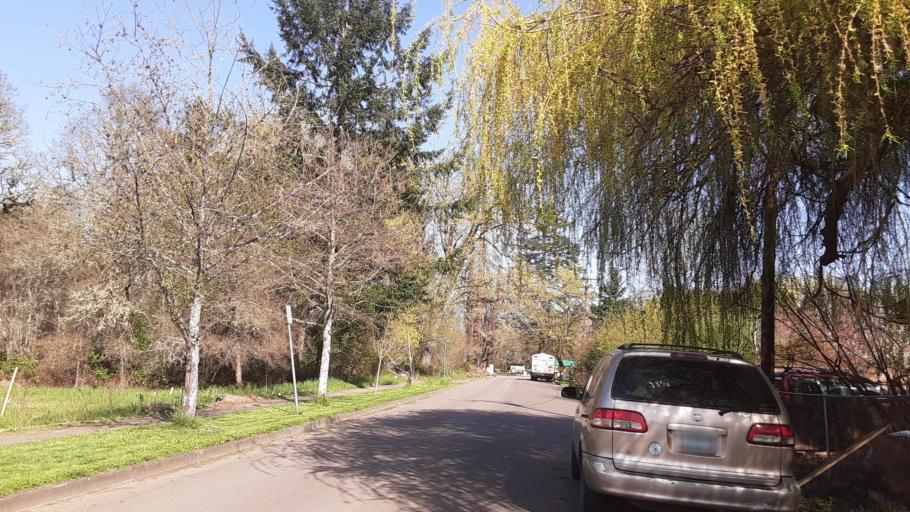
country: US
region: Oregon
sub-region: Benton County
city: Corvallis
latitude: 44.5452
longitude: -123.2553
